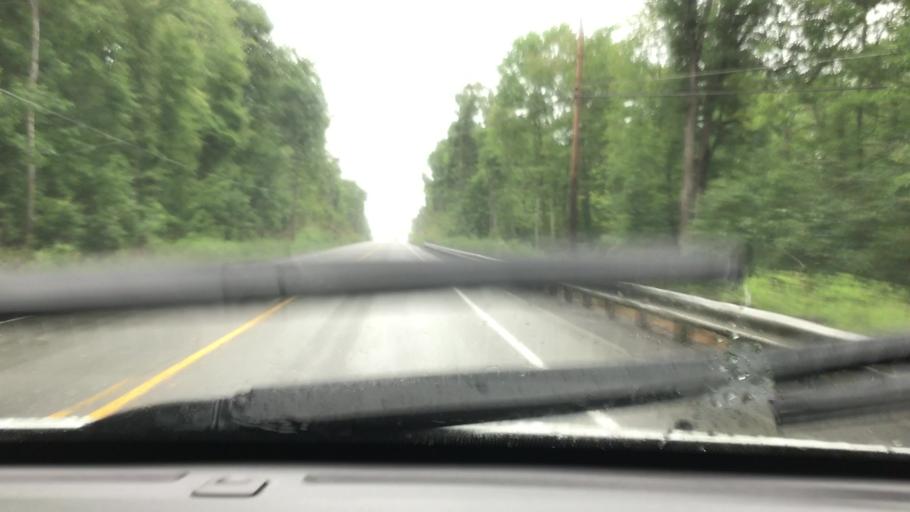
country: US
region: Pennsylvania
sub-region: Clearfield County
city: Osceola Mills
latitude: 40.8358
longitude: -78.2236
